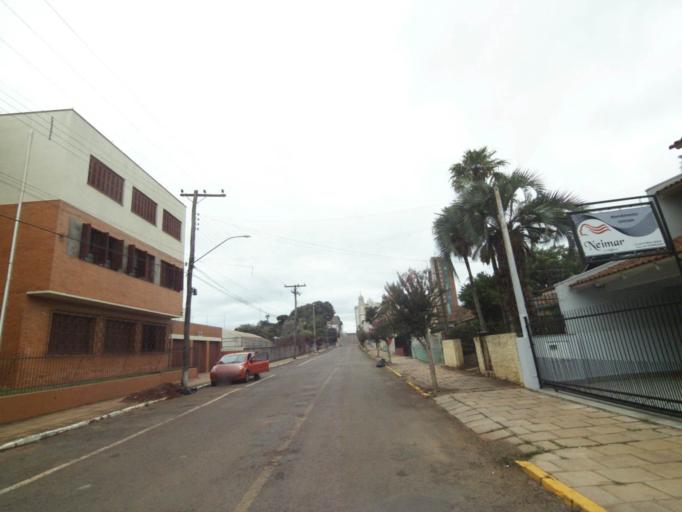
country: BR
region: Rio Grande do Sul
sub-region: Lagoa Vermelha
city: Lagoa Vermelha
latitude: -28.2116
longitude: -51.5282
